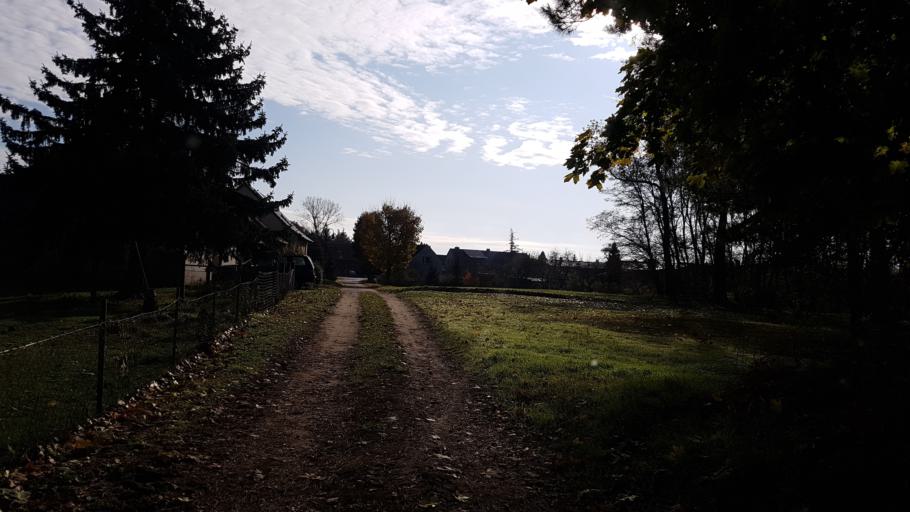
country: DE
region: Brandenburg
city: Doberlug-Kirchhain
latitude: 51.6933
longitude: 13.5130
